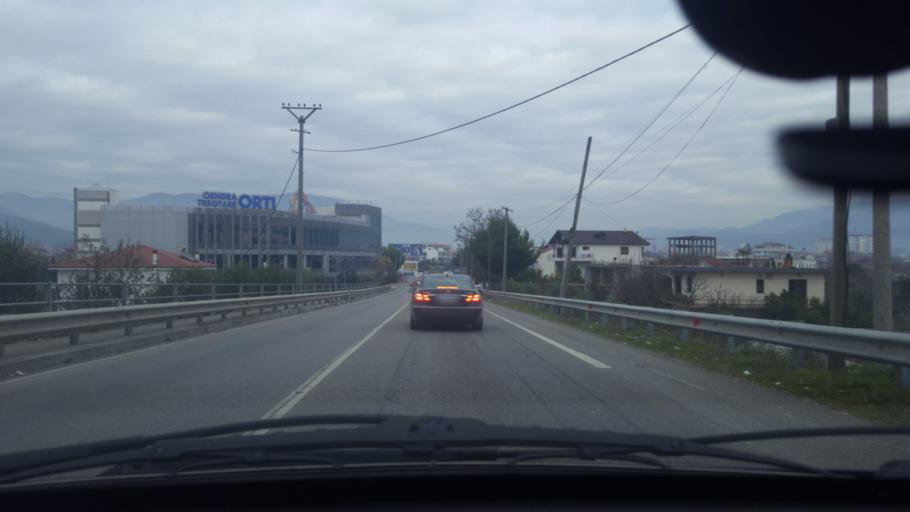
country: AL
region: Elbasan
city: Elbasan
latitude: 41.1040
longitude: 20.0599
